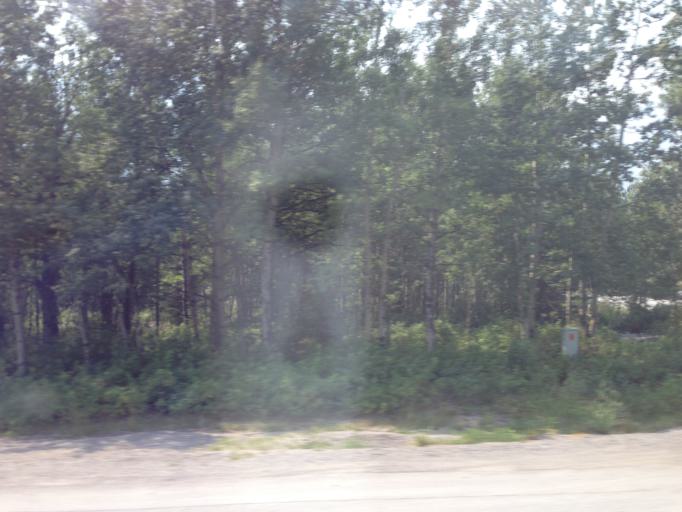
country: CA
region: Alberta
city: Canmore
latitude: 51.0781
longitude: -115.3390
